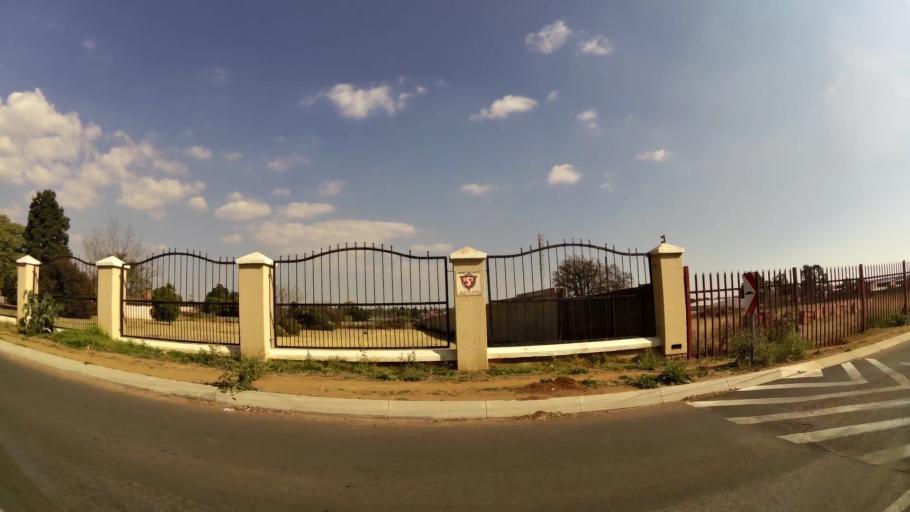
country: ZA
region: Gauteng
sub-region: City of Johannesburg Metropolitan Municipality
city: Modderfontein
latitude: -26.0834
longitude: 28.2570
